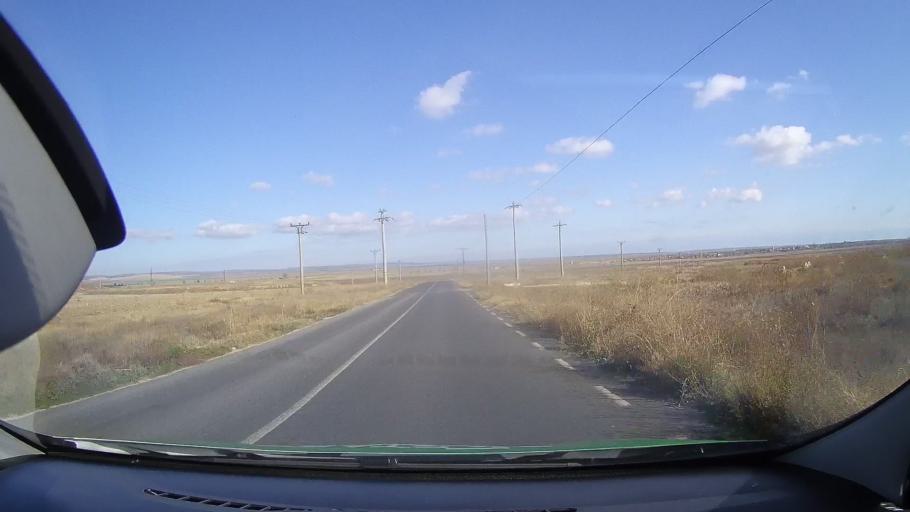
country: RO
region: Tulcea
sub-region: Comuna Ceamurlia de Jos
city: Ceamurlia de Jos
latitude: 44.7418
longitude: 28.6959
